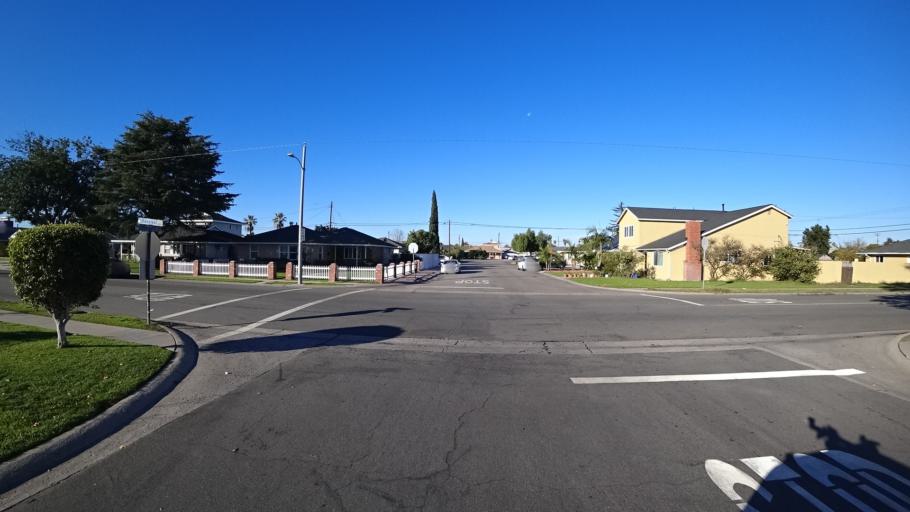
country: US
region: California
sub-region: Orange County
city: Garden Grove
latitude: 33.7686
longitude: -117.9612
